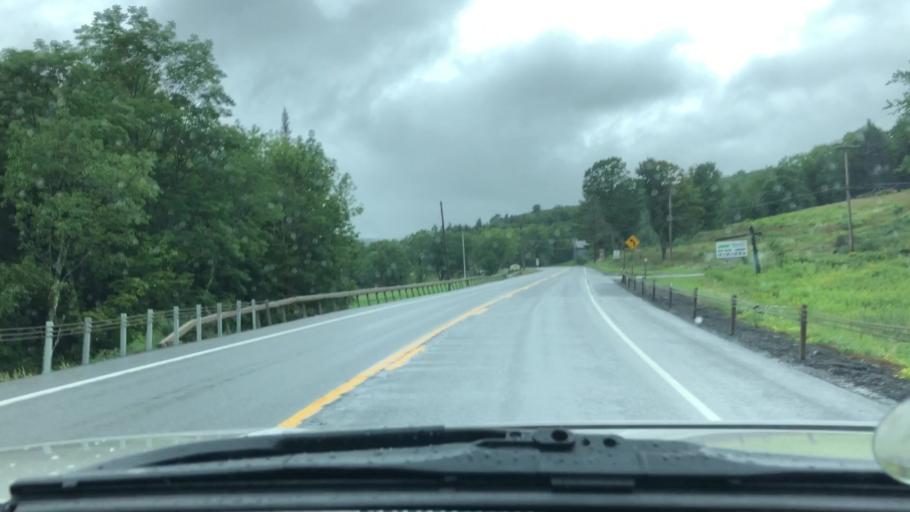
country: US
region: New York
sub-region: Greene County
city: Cairo
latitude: 42.3044
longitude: -74.2168
